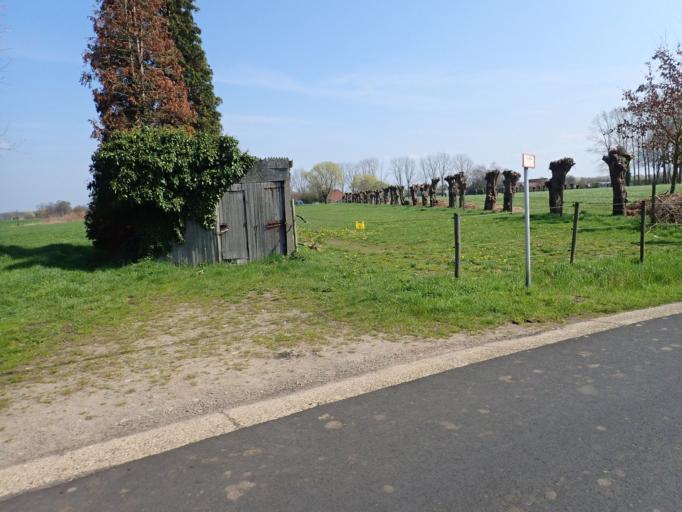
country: BE
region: Flanders
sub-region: Provincie Antwerpen
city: Berlaar
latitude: 51.1034
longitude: 4.6621
